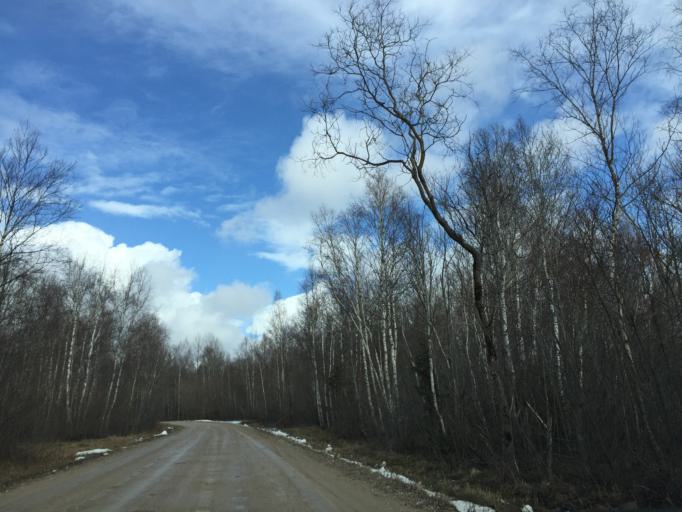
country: EE
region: Laeaene
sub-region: Lihula vald
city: Lihula
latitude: 58.7211
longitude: 23.8290
